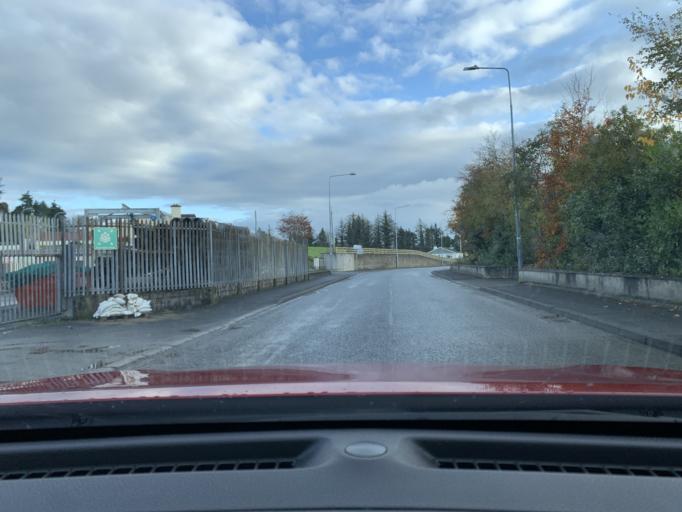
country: IE
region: Ulster
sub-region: County Donegal
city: Ballybofey
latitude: 54.8019
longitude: -7.7726
